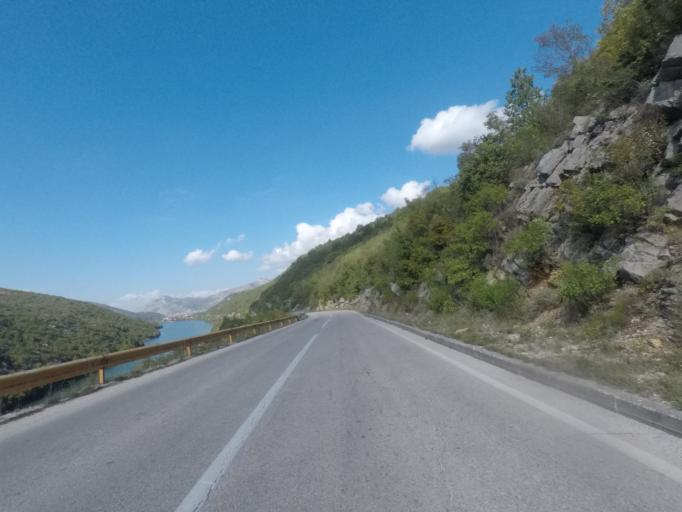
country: BA
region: Republika Srpska
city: Trebinje
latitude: 42.7021
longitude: 18.4206
